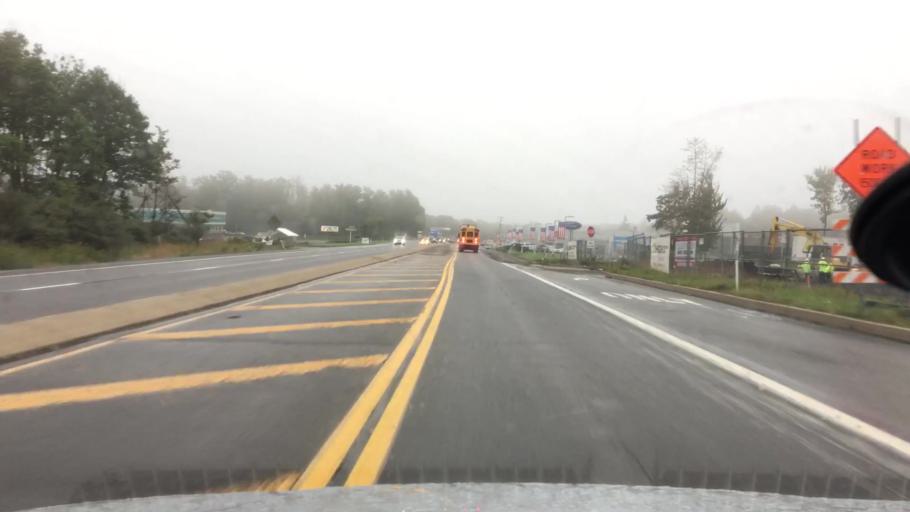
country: US
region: Pennsylvania
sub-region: Monroe County
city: Mount Pocono
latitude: 41.1166
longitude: -75.3819
